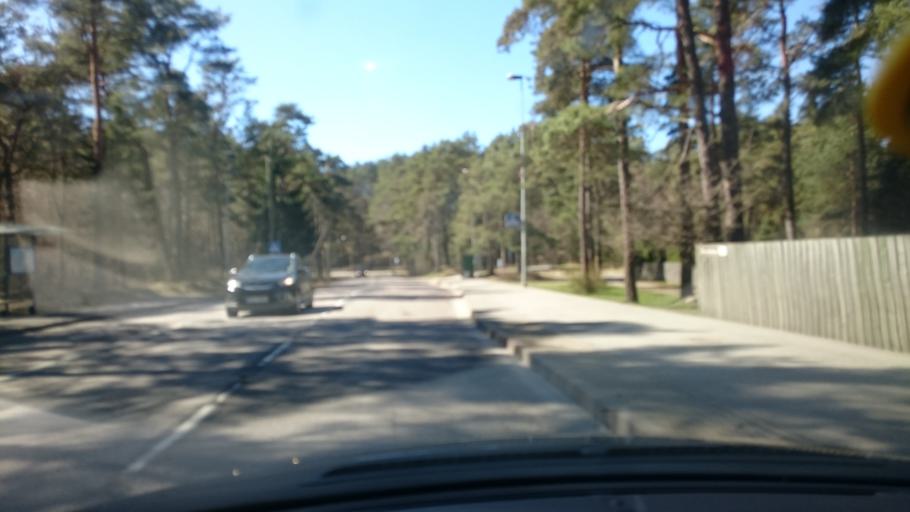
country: EE
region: Harju
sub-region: Tallinna linn
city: Kose
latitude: 59.4714
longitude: 24.8779
